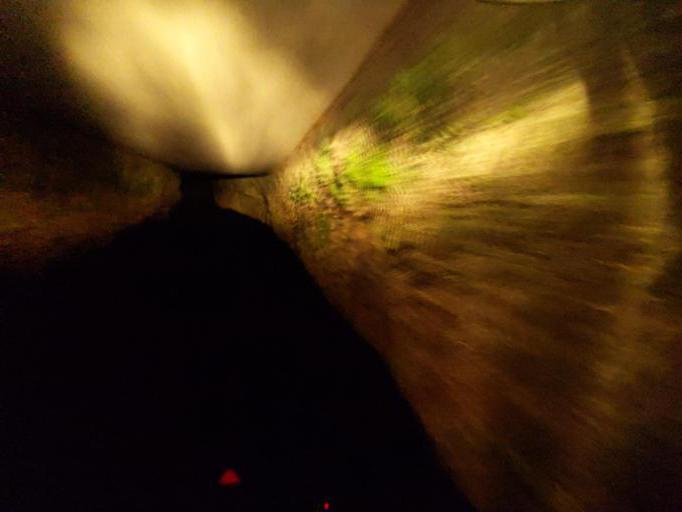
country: GB
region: England
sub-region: Cornwall
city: Torpoint
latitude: 50.3478
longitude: -4.2263
